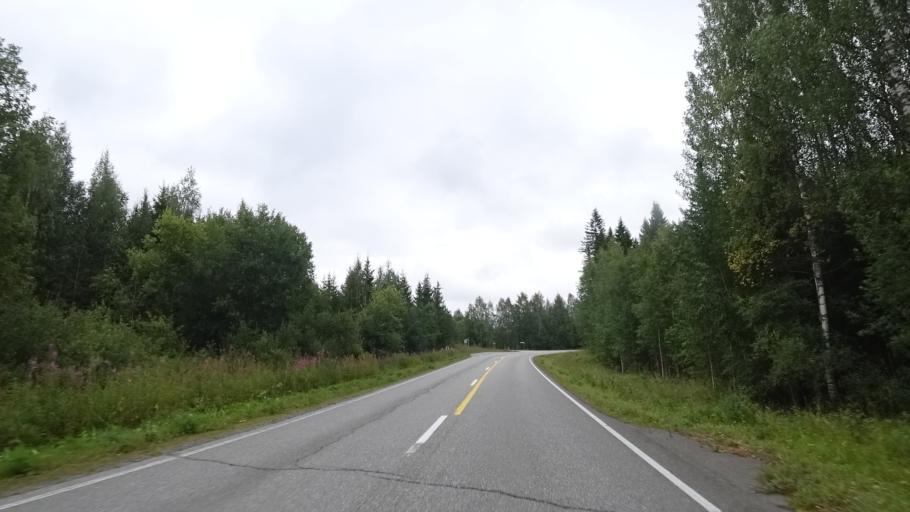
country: FI
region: North Karelia
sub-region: Pielisen Karjala
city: Lieksa
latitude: 63.2804
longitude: 30.6121
